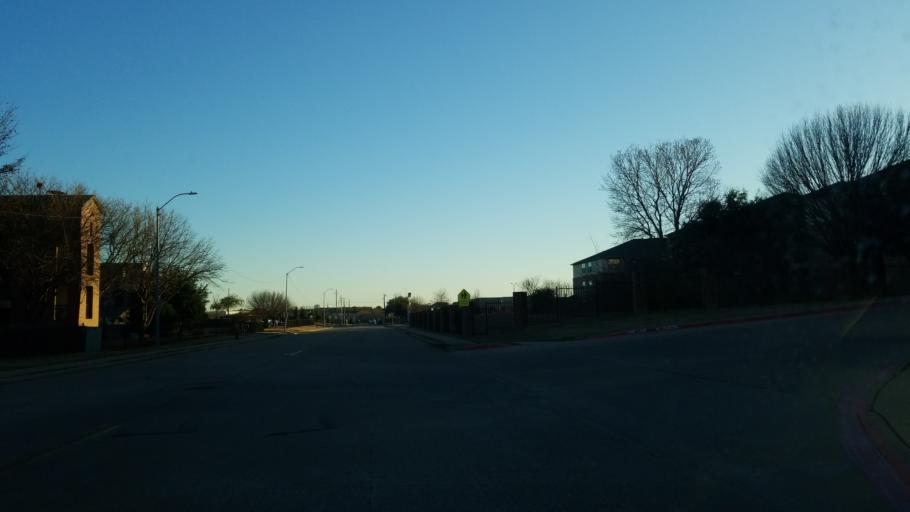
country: US
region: Texas
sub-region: Tarrant County
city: Arlington
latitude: 32.7311
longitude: -97.0541
